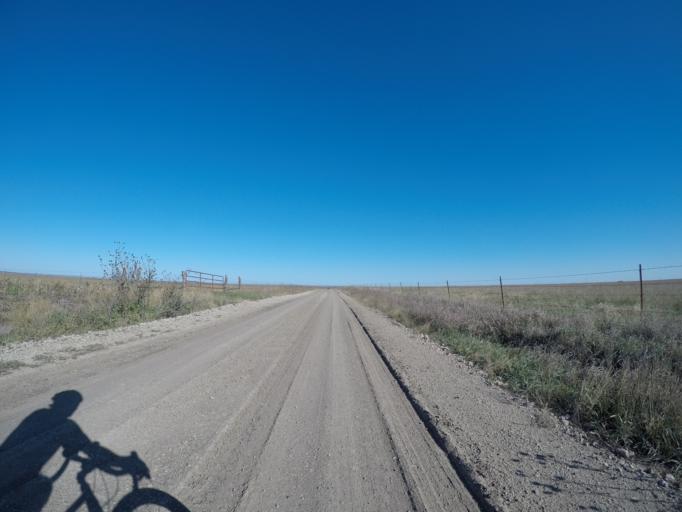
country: US
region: Kansas
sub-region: Wabaunsee County
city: Alma
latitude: 38.8811
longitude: -96.4096
